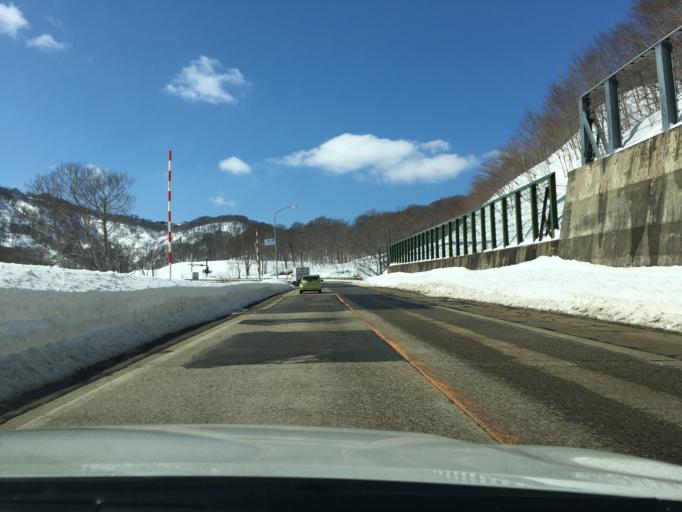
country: JP
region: Yamagata
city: Tsuruoka
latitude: 38.4936
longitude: 139.9773
